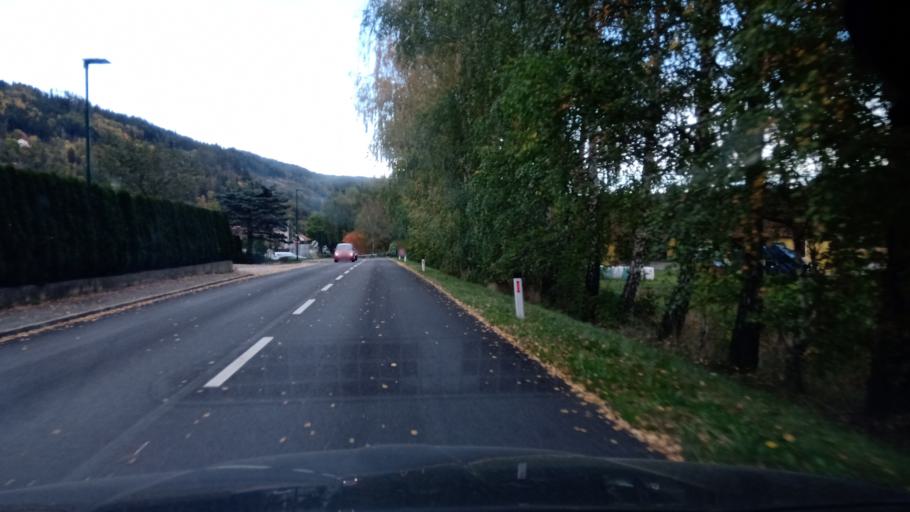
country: AT
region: Styria
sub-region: Politischer Bezirk Leoben
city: Proleb
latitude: 47.3950
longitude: 15.1322
